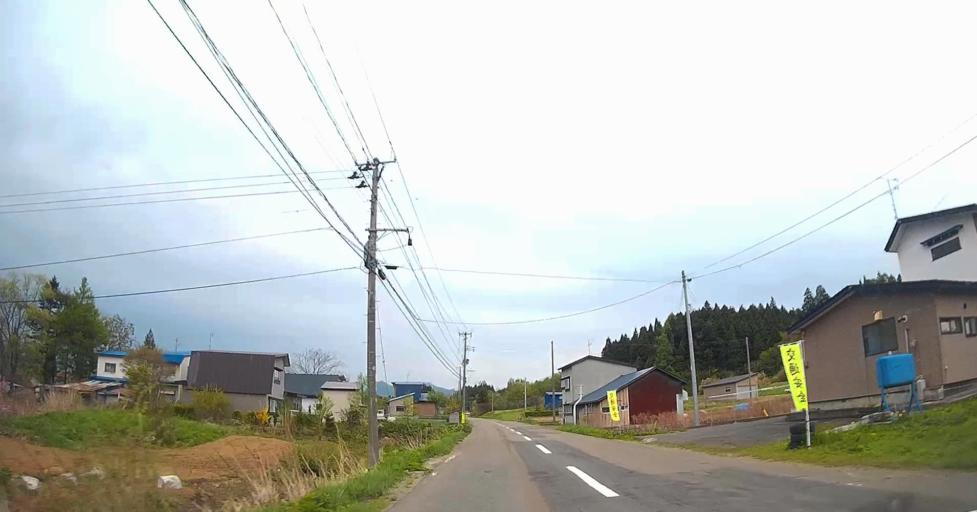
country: JP
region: Aomori
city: Shimokizukuri
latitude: 41.1793
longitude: 140.4649
